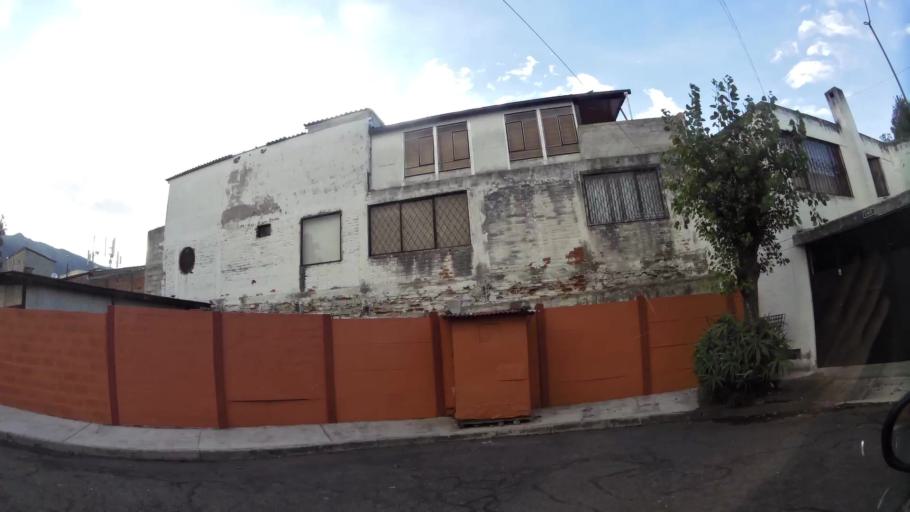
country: EC
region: Pichincha
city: Quito
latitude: -0.1556
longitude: -78.4814
